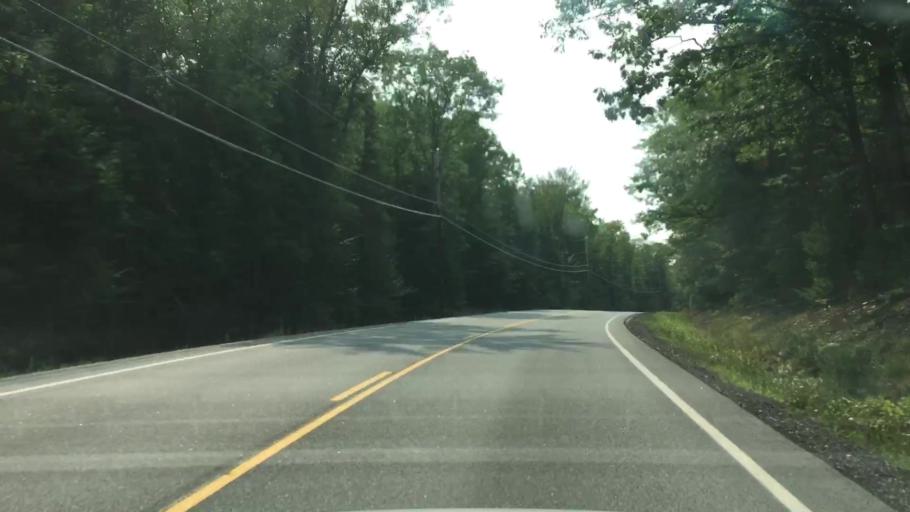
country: US
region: Maine
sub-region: Oxford County
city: Paris
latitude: 44.2366
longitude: -70.4780
